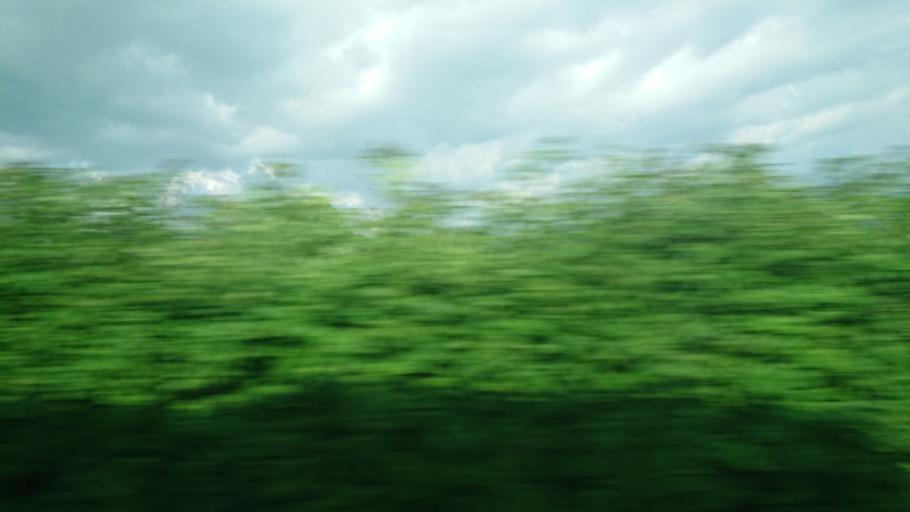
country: GB
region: England
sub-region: North Yorkshire
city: High Bentham
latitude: 54.1342
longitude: -2.5112
